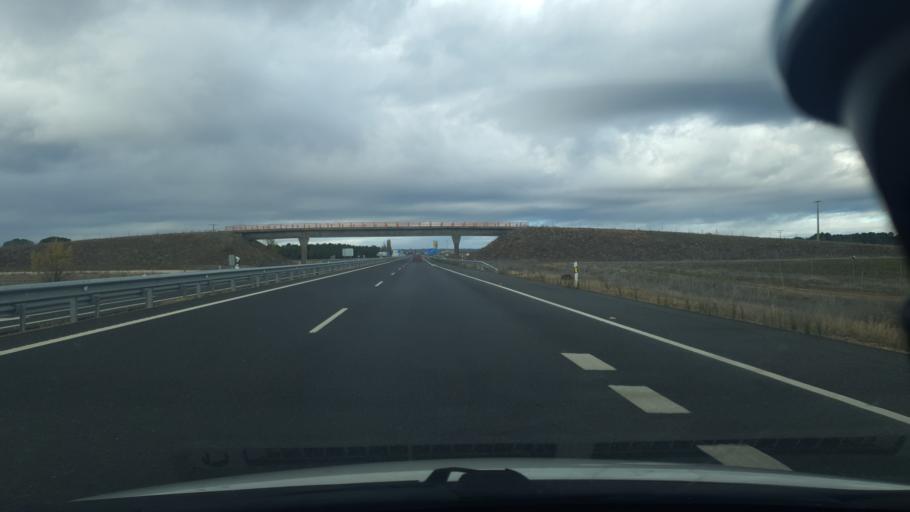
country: ES
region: Castille and Leon
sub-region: Provincia de Segovia
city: Sanchonuno
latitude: 41.2998
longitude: -4.3011
